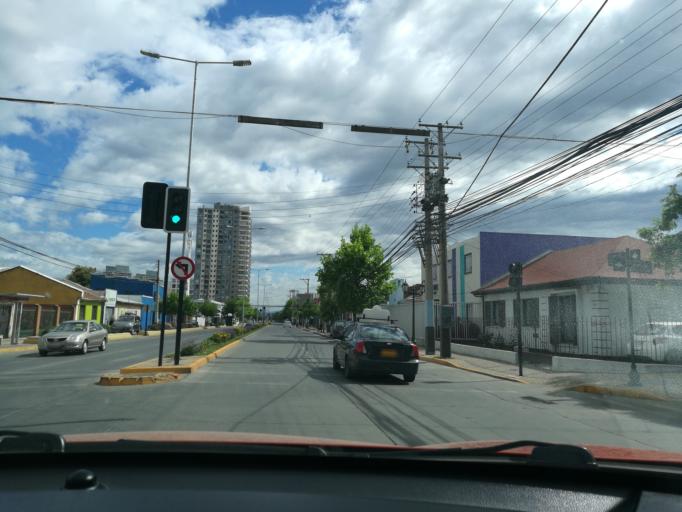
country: CL
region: O'Higgins
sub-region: Provincia de Cachapoal
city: Rancagua
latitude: -34.1735
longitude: -70.7358
